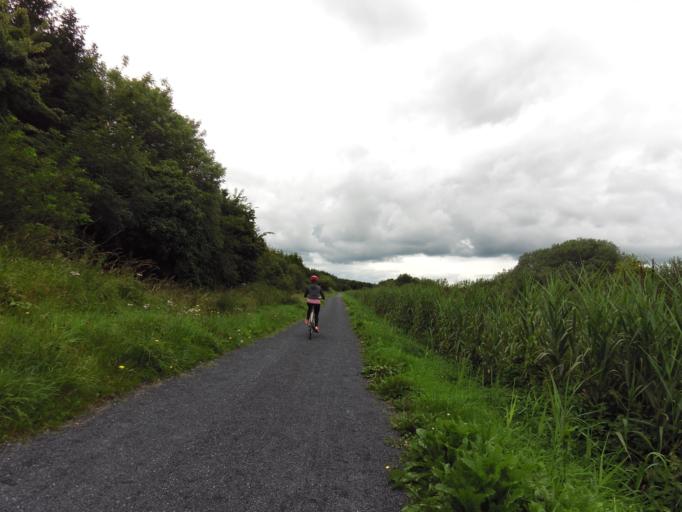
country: IE
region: Leinster
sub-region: An Iarmhi
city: An Muileann gCearr
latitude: 53.5186
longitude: -7.4361
